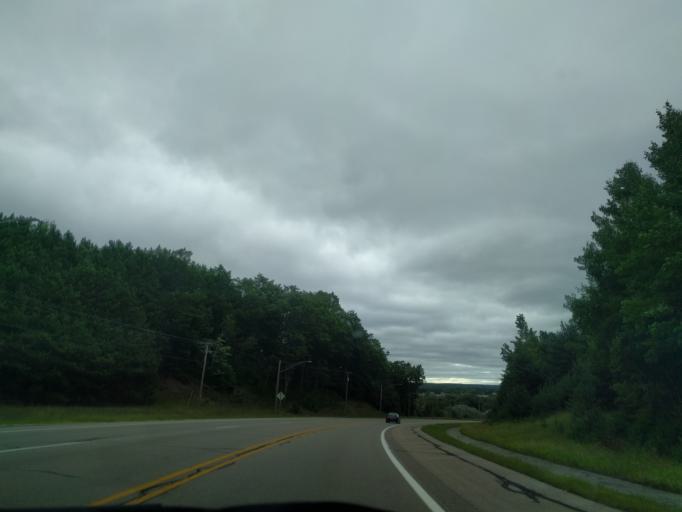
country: US
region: Michigan
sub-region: Delta County
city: Gladstone
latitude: 45.8559
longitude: -87.0373
